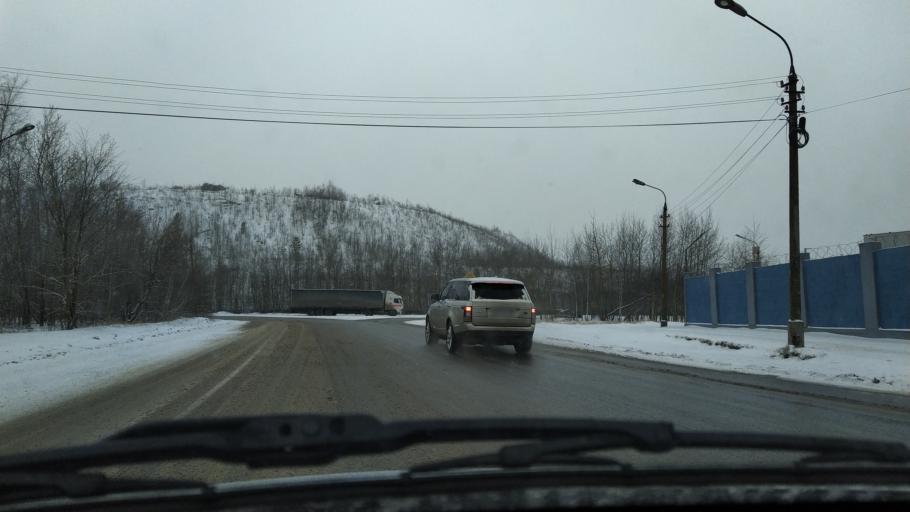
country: RU
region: Moskovskaya
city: Lopatinskiy
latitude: 55.2967
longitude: 38.7177
